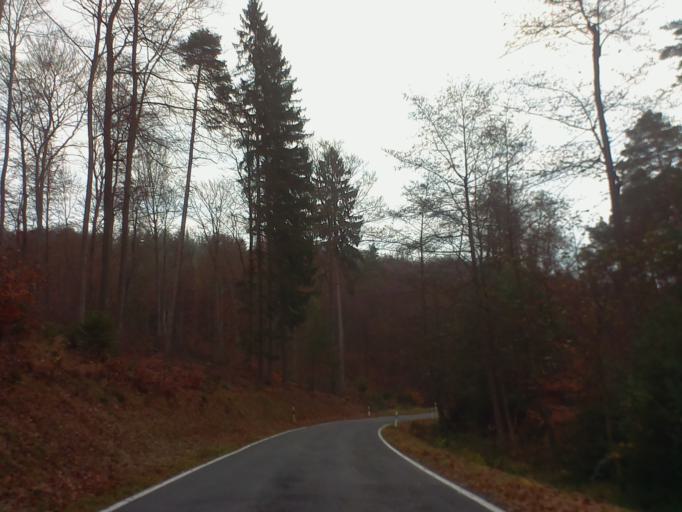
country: DE
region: Rheinland-Pfalz
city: Altleiningen
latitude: 49.4795
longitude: 8.0743
